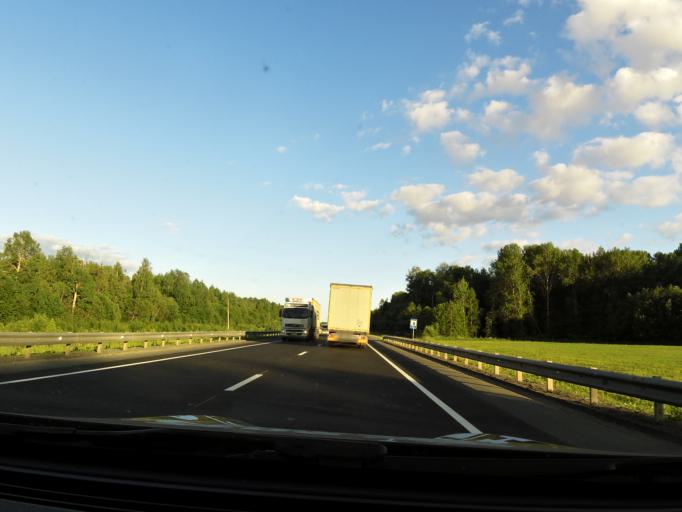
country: RU
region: Vologda
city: Gryazovets
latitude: 58.9815
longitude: 40.1445
